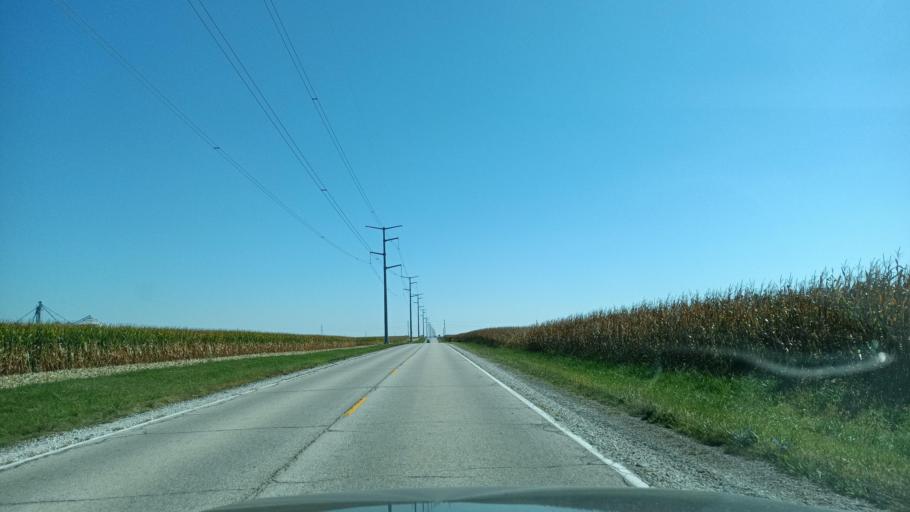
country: US
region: Illinois
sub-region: Peoria County
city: Elmwood
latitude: 40.9023
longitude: -90.0225
